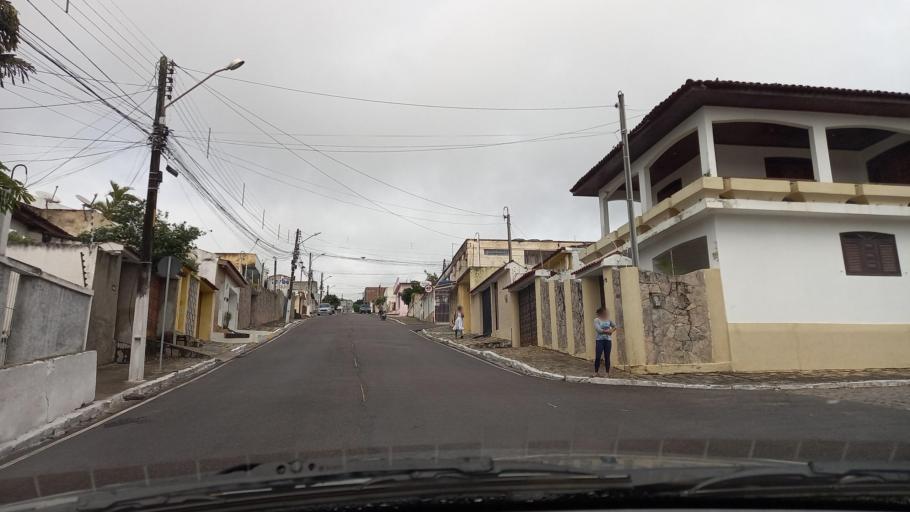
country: BR
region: Pernambuco
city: Garanhuns
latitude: -8.8944
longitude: -36.4918
